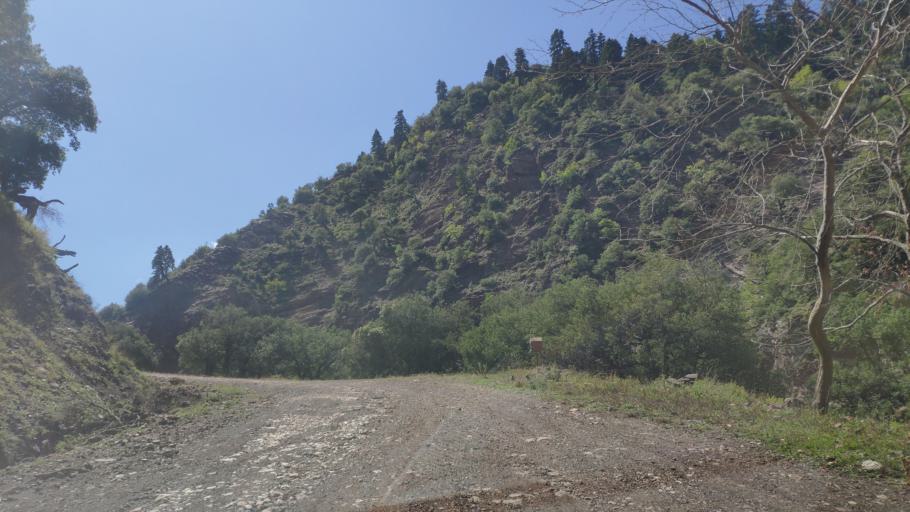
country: GR
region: Central Greece
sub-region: Nomos Evrytanias
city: Kerasochori
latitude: 39.1419
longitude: 21.6582
